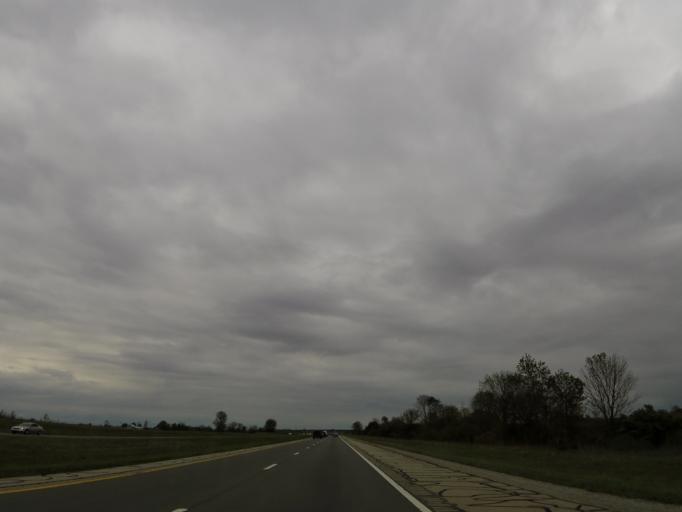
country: US
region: Ohio
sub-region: Madison County
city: Bethel
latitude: 39.7314
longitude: -83.3671
